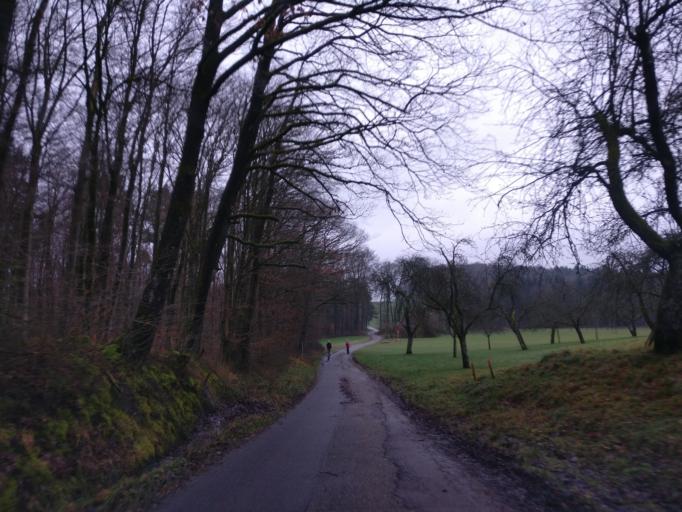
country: DE
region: Baden-Wuerttemberg
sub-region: Regierungsbezirk Stuttgart
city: Rudersberg
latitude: 48.8763
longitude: 9.4946
